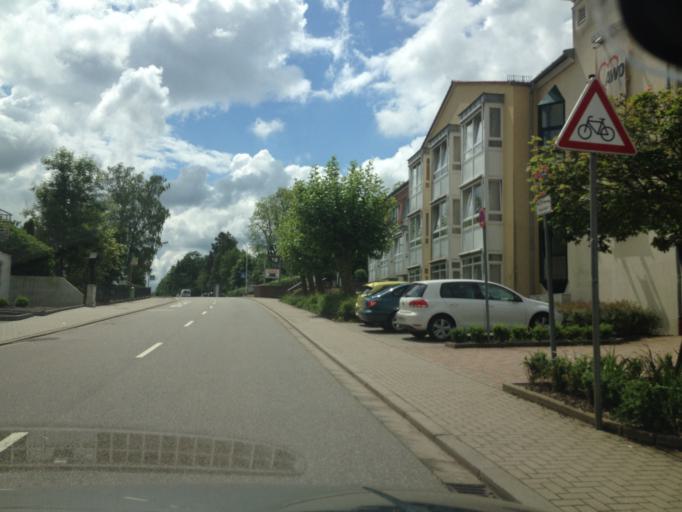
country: DE
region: Saarland
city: Bexbach
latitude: 49.3432
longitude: 7.2616
